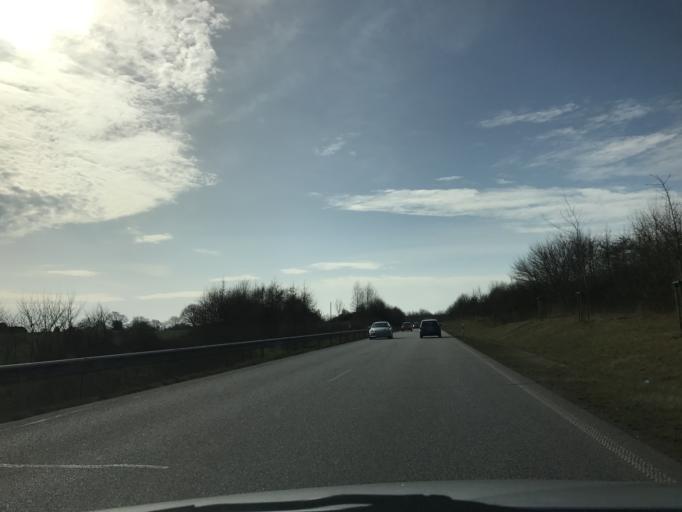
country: DE
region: Schleswig-Holstein
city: Klein Wittensee
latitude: 54.3965
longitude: 9.7374
